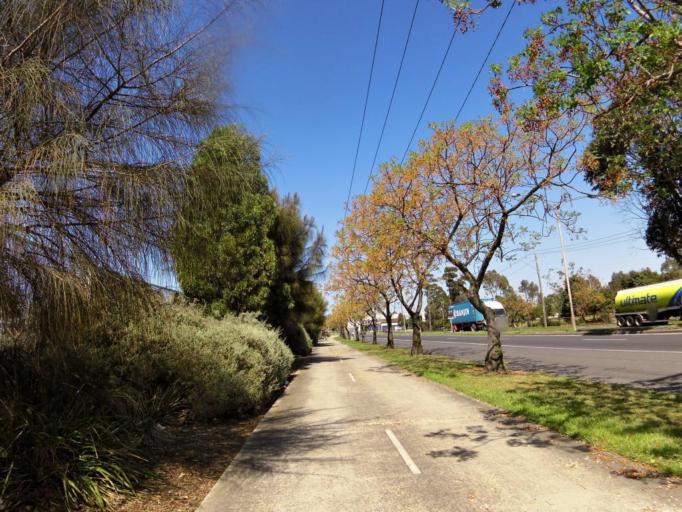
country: AU
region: Victoria
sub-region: Maribyrnong
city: Yarraville
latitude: -37.8130
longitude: 144.9008
